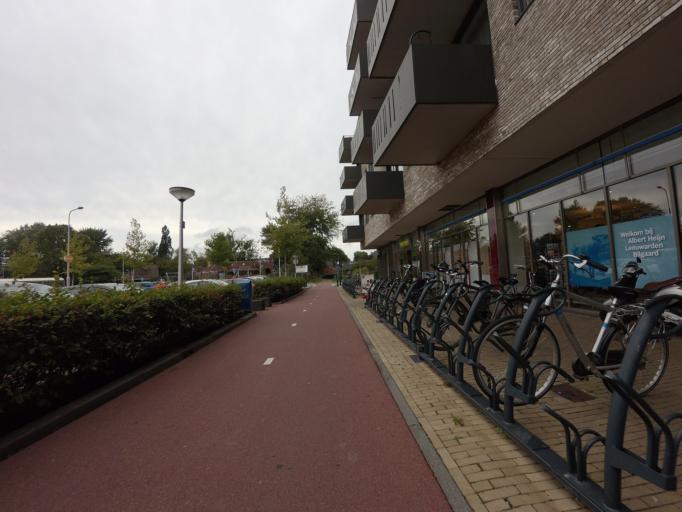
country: NL
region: Friesland
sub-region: Gemeente Leeuwarden
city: Bilgaard
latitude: 53.2152
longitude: 5.7927
